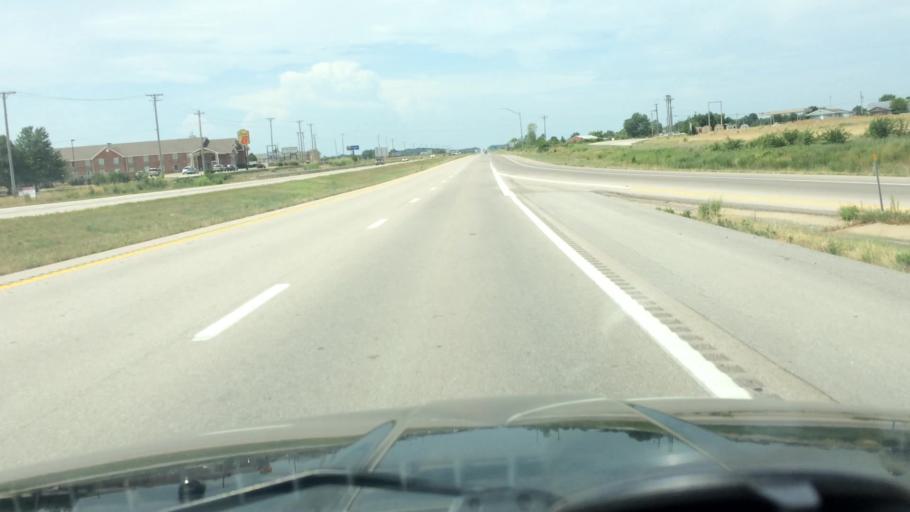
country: US
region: Missouri
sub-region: Polk County
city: Bolivar
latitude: 37.5953
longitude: -93.4343
